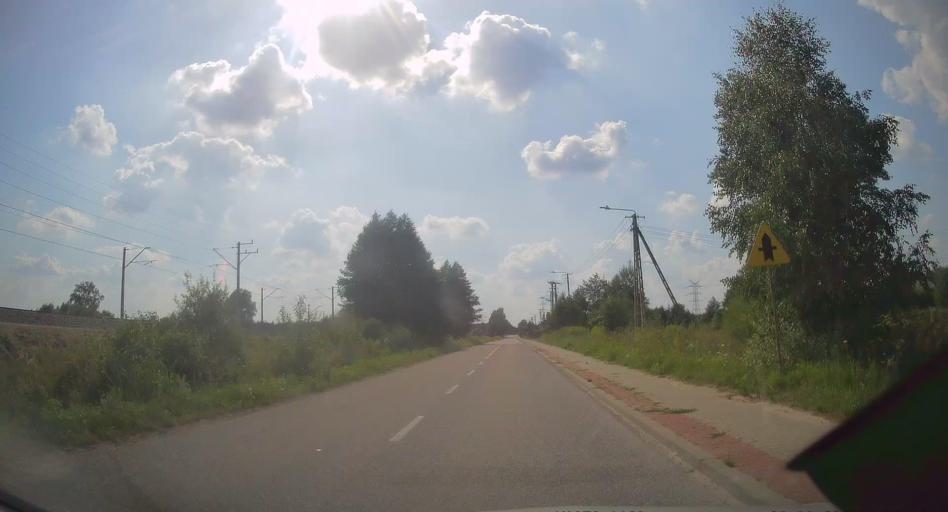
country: PL
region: Swietokrzyskie
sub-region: Powiat jedrzejowski
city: Malogoszcz
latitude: 50.8667
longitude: 20.3176
